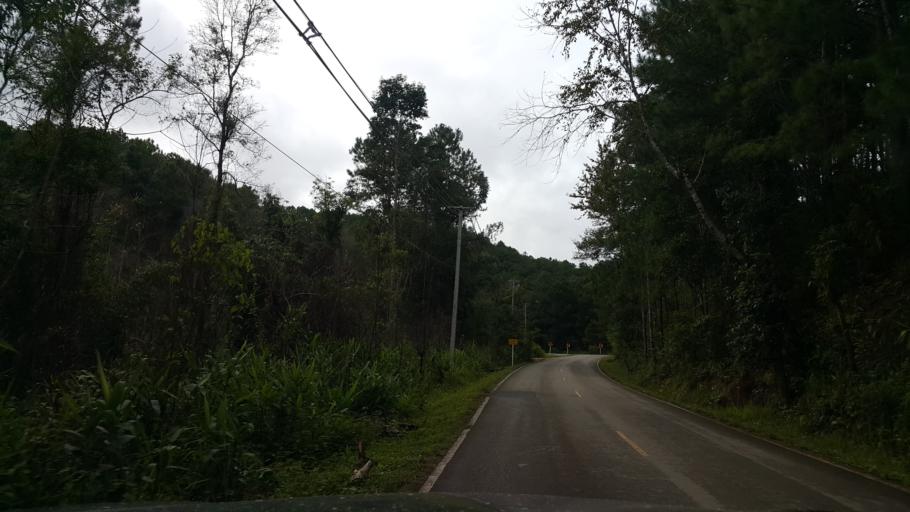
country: TH
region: Chiang Mai
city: Samoeng
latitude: 18.8871
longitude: 98.5008
